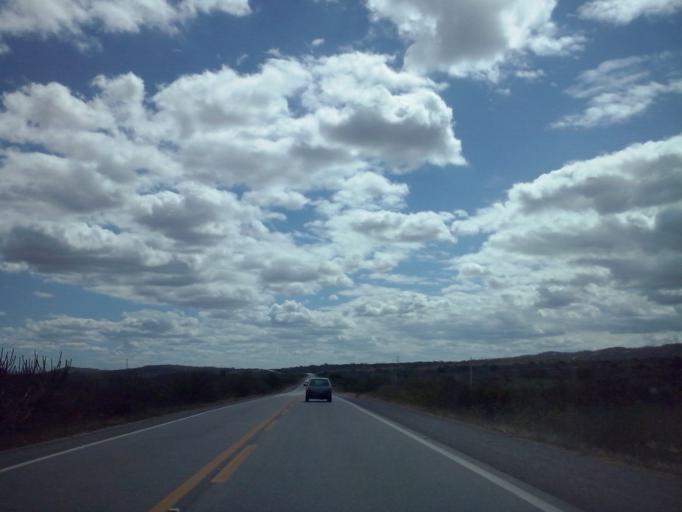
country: BR
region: Paraiba
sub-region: Soledade
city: Soledade
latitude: -7.0478
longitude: -36.3876
